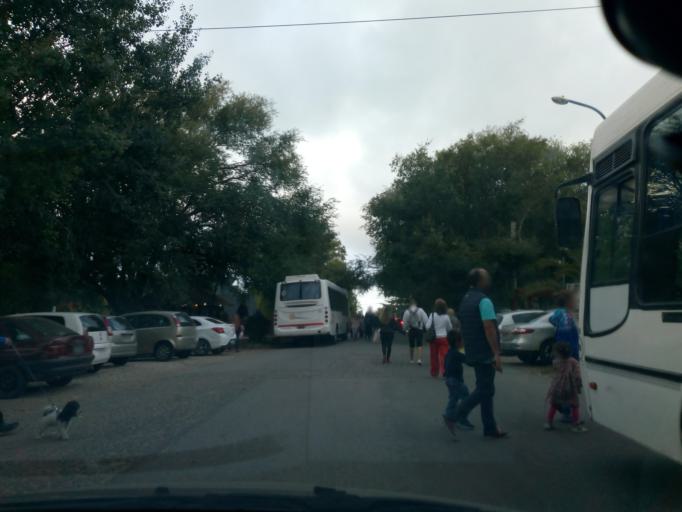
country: AR
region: Buenos Aires
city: Mar del Plata
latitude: -37.9459
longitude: -57.7786
